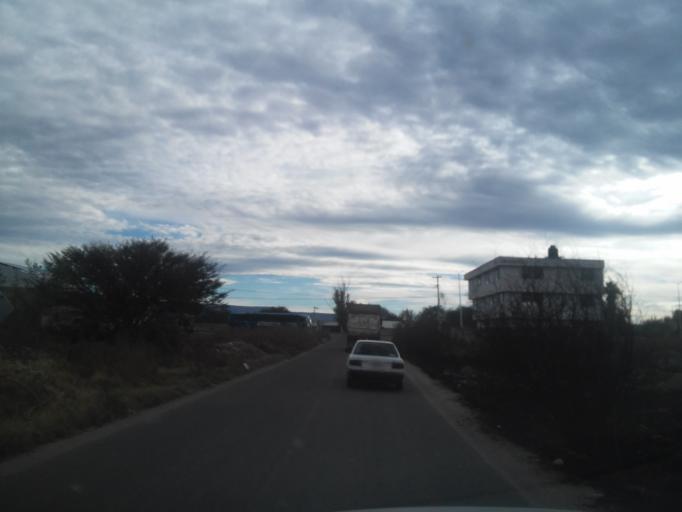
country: MX
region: Durango
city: Victoria de Durango
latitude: 24.0276
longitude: -104.5751
